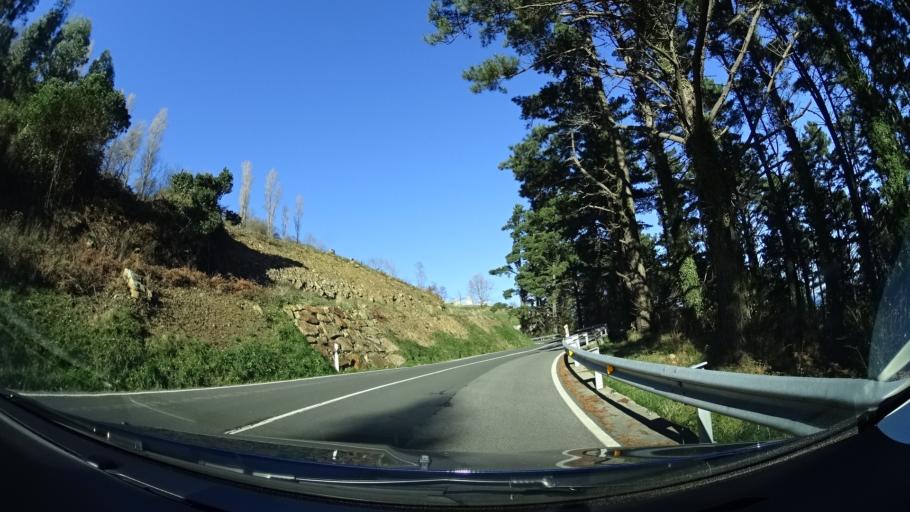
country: ES
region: Basque Country
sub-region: Bizkaia
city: Bermeo
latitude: 43.4426
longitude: -2.7547
